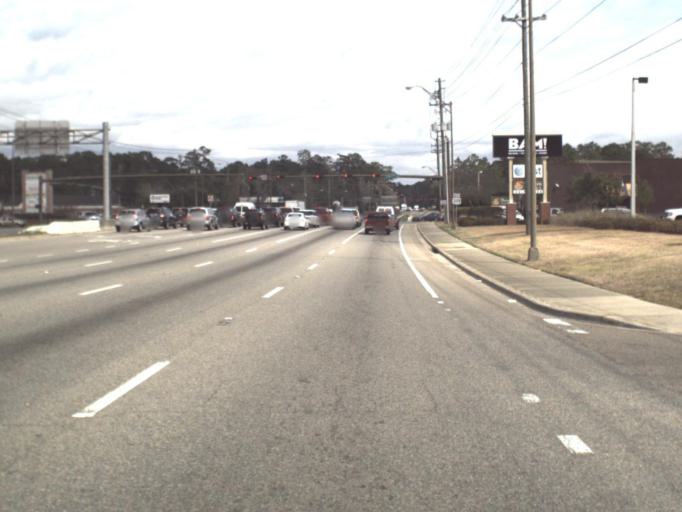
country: US
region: Florida
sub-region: Leon County
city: Tallahassee
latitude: 30.5091
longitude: -84.2480
